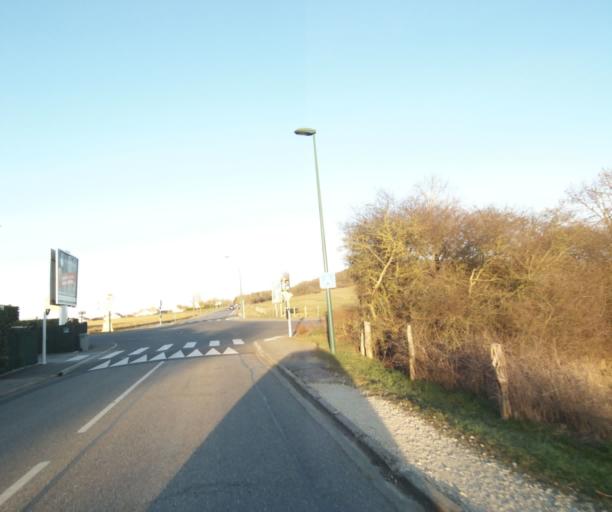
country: FR
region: Lorraine
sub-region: Departement de Meurthe-et-Moselle
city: Saulxures-les-Nancy
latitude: 48.6927
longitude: 6.2506
